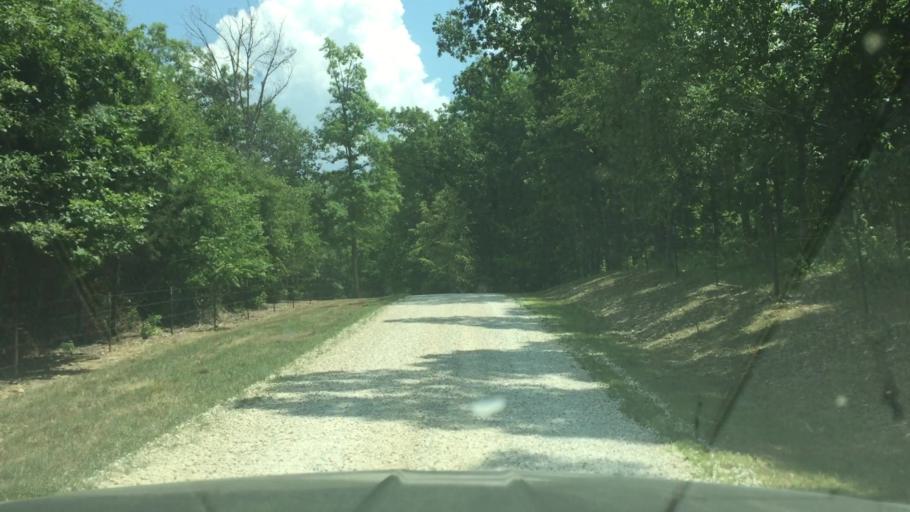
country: US
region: Missouri
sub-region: Miller County
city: Tuscumbia
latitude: 38.1310
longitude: -92.4450
